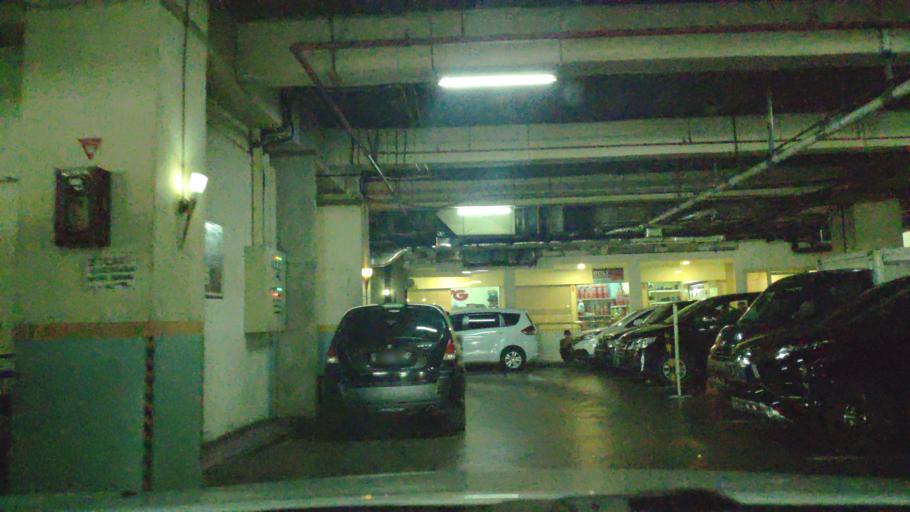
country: ID
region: Jakarta Raya
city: Jakarta
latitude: -6.1457
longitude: 106.8175
